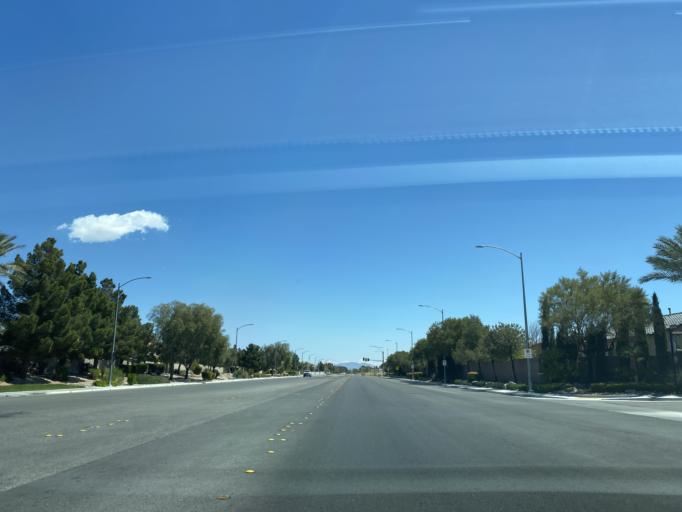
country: US
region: Nevada
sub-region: Clark County
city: North Las Vegas
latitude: 36.3051
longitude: -115.2379
